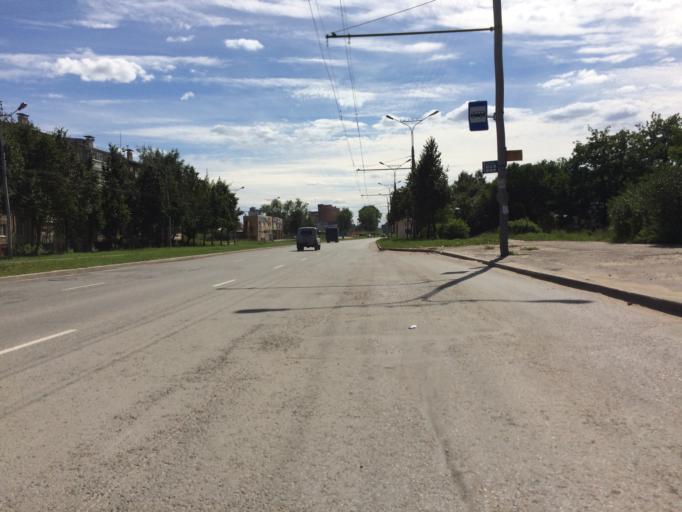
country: RU
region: Mariy-El
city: Yoshkar-Ola
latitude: 56.6318
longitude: 47.9391
